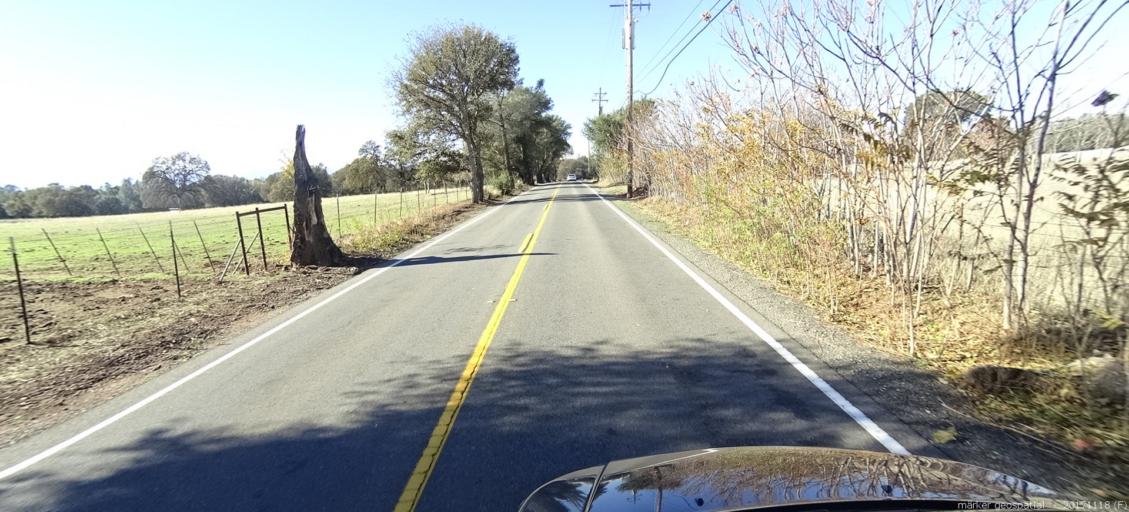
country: US
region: California
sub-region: Shasta County
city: Cottonwood
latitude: 40.3890
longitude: -122.3664
